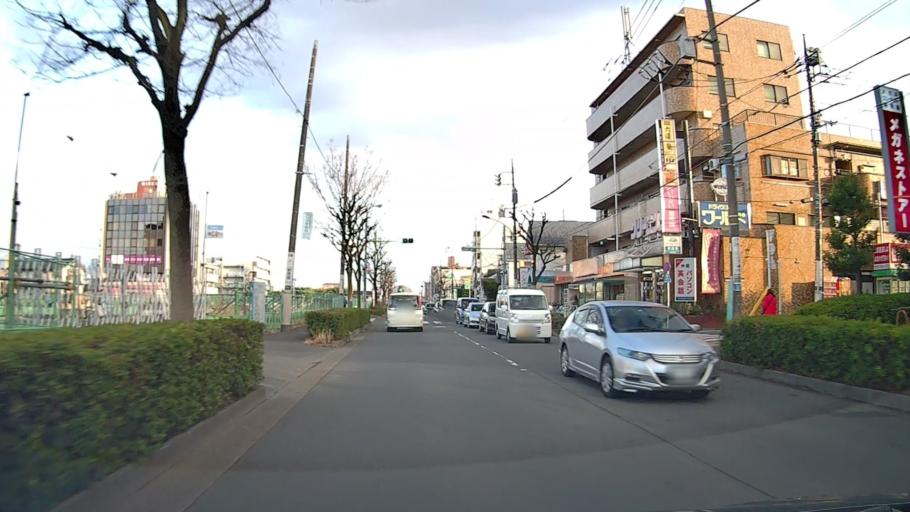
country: JP
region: Saitama
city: Wako
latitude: 35.7572
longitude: 139.6549
